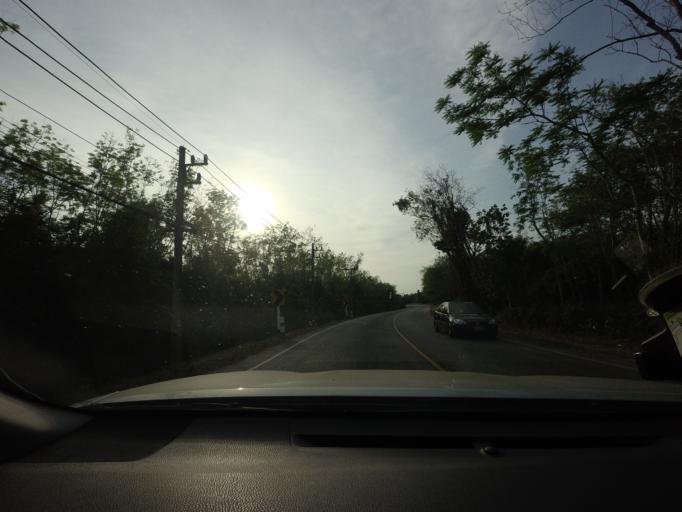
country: TH
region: Narathiwat
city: Ra-ngae
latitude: 6.3371
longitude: 101.7171
